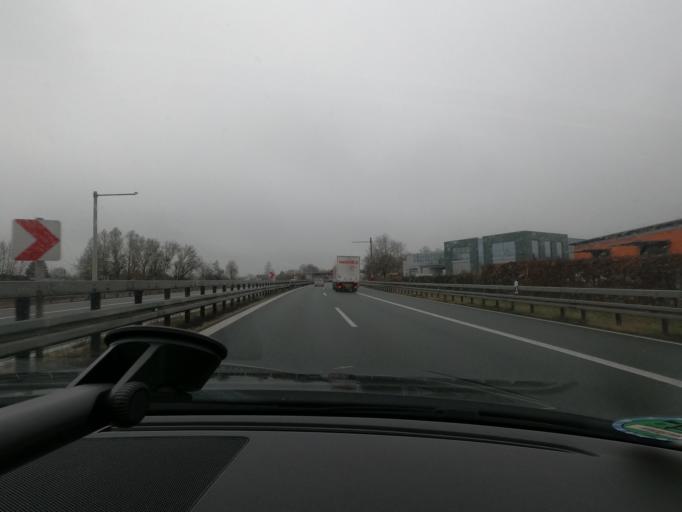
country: DE
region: Bavaria
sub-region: Regierungsbezirk Mittelfranken
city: Baiersdorf
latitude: 49.6525
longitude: 11.0322
